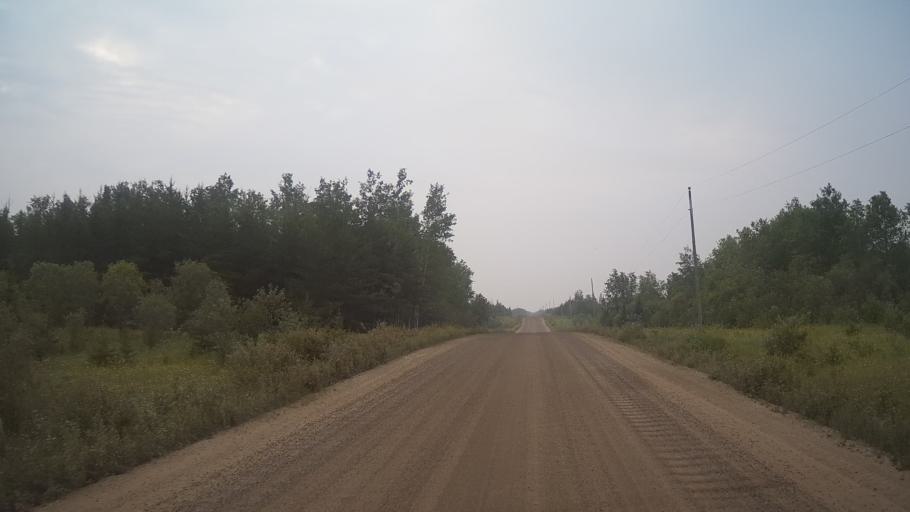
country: CA
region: Ontario
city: Hearst
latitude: 49.6345
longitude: -83.2783
